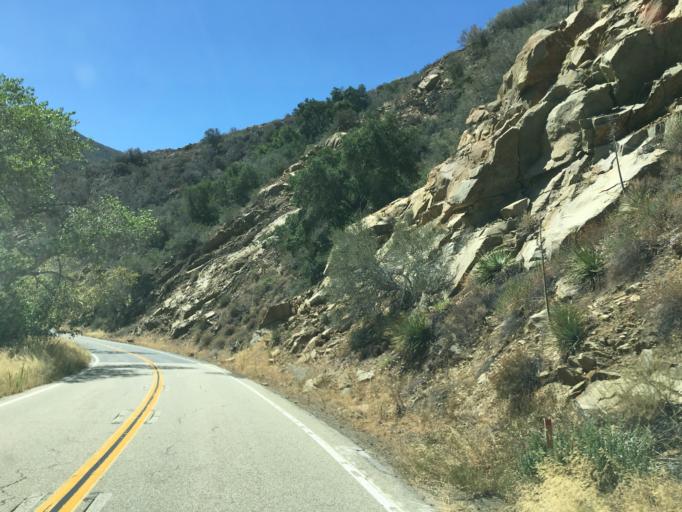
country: US
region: California
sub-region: Los Angeles County
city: Castaic
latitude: 34.5816
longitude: -118.5578
